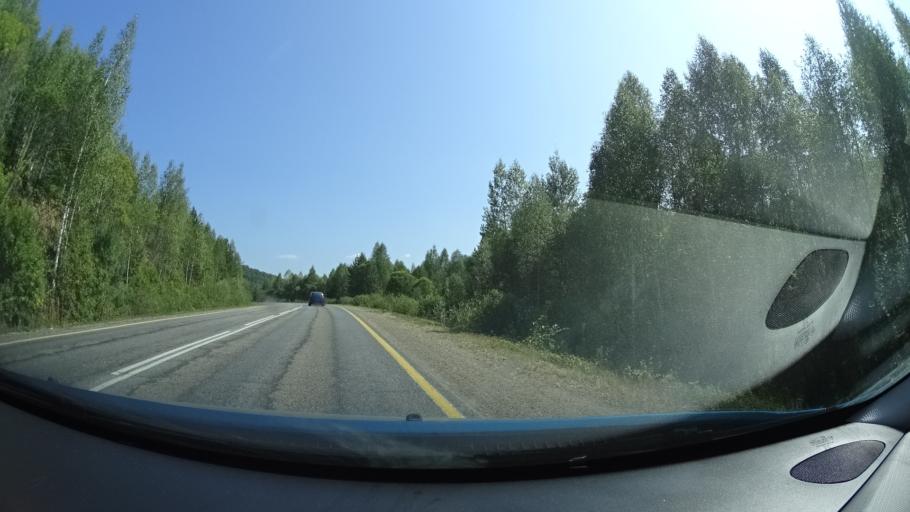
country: RU
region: Bashkortostan
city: Inzer
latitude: 54.3374
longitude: 57.1024
